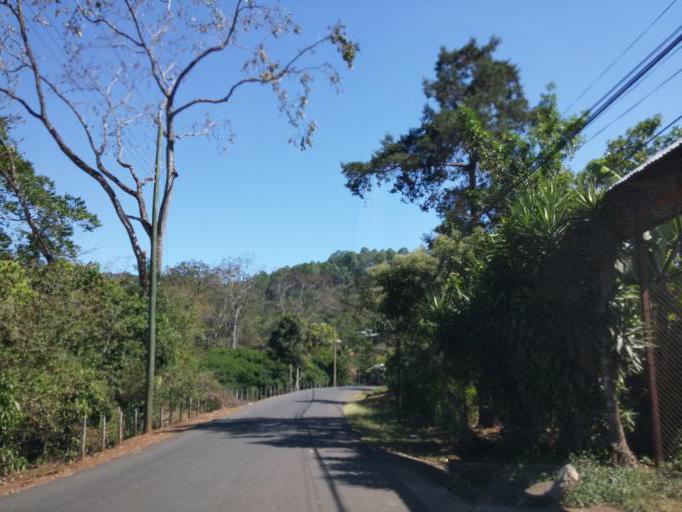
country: CR
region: San Jose
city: Palmichal
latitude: 9.8396
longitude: -84.2114
